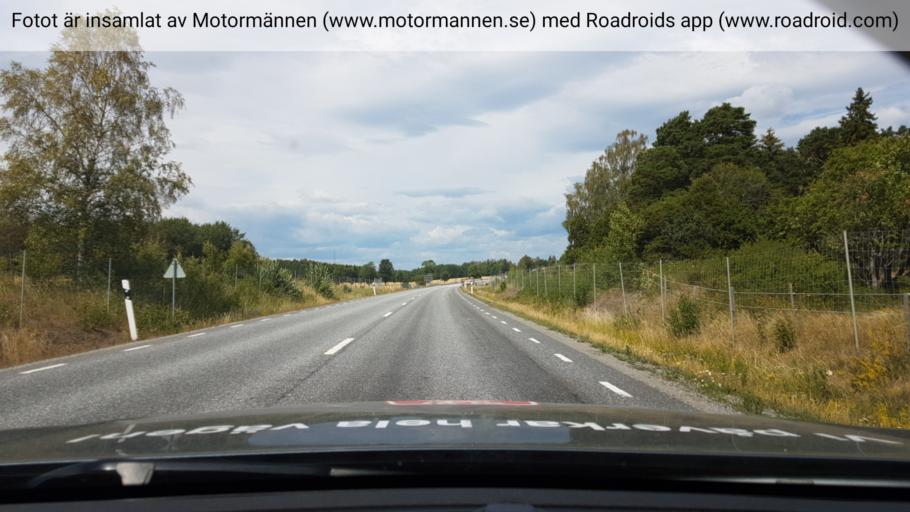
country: SE
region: Stockholm
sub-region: Upplands-Bro Kommun
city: Bro
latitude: 59.5967
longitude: 17.6138
